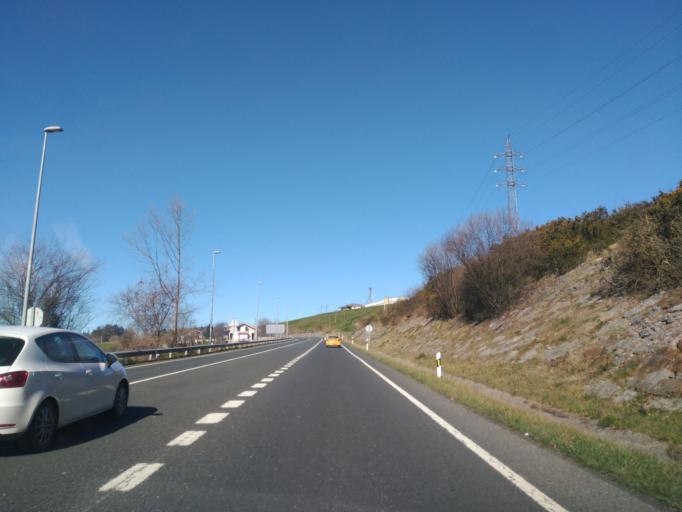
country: ES
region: Cantabria
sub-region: Provincia de Cantabria
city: Cabezon de la Sal
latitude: 43.3128
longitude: -4.2450
